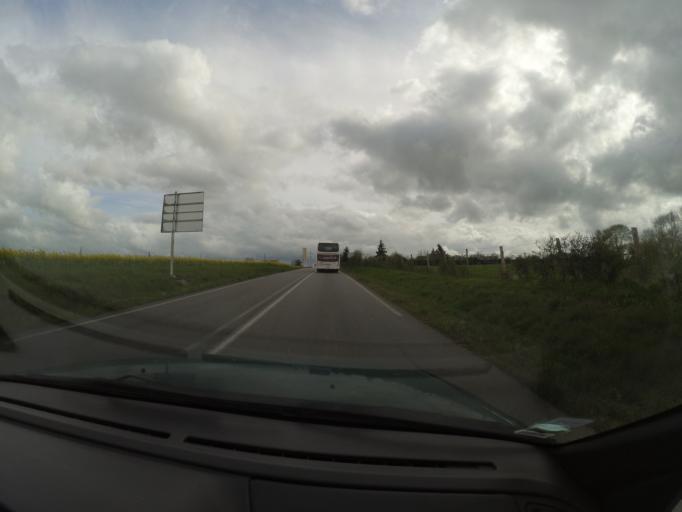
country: FR
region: Pays de la Loire
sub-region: Departement de Maine-et-Loire
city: Lire
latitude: 47.3282
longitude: -1.1671
